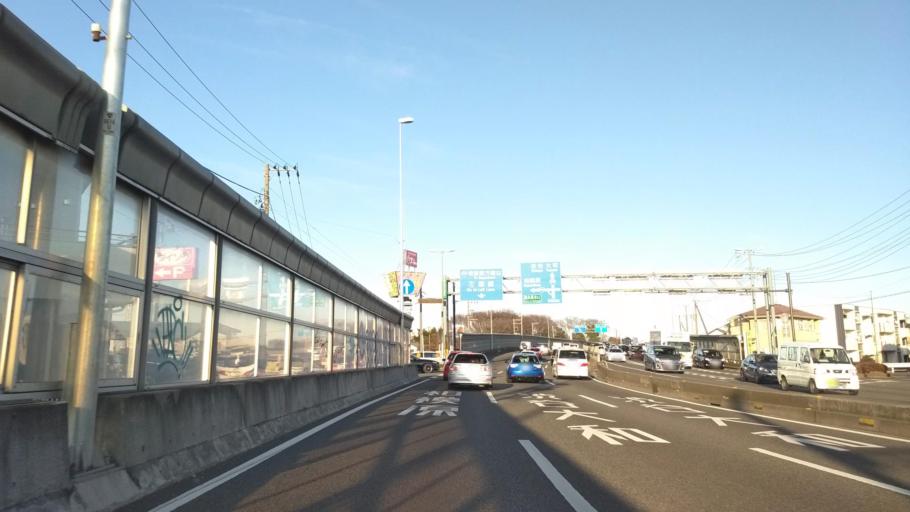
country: JP
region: Kanagawa
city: Atsugi
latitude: 35.4633
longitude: 139.3604
